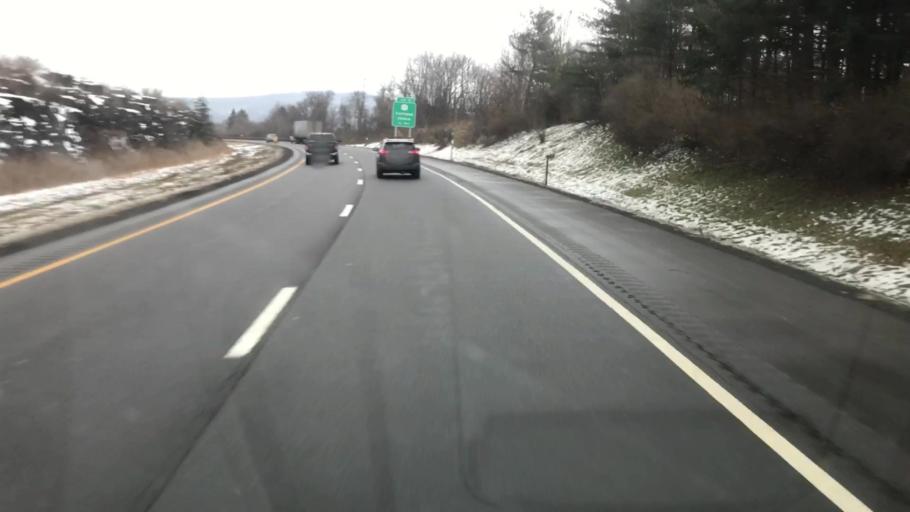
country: US
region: New York
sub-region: Cortland County
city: Cortland
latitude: 42.6120
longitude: -76.1810
